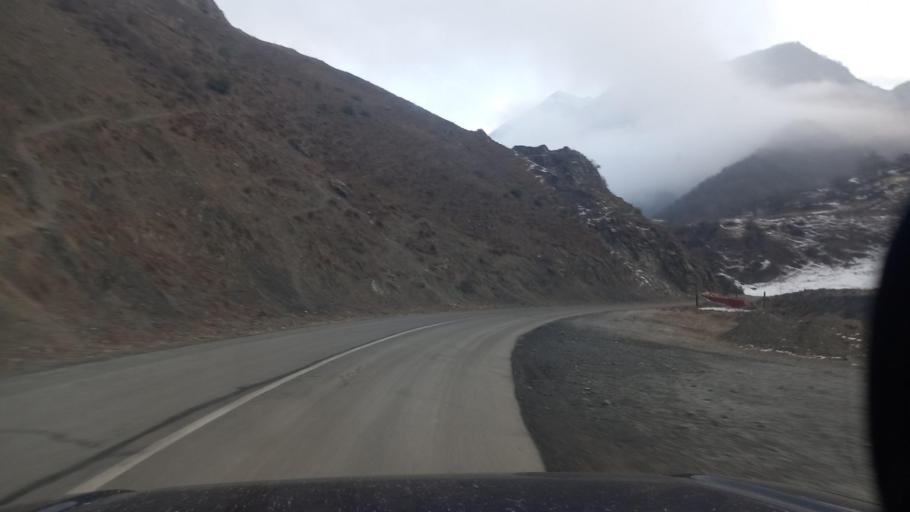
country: RU
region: Ingushetiya
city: Dzhayrakh
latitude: 42.8010
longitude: 44.7583
